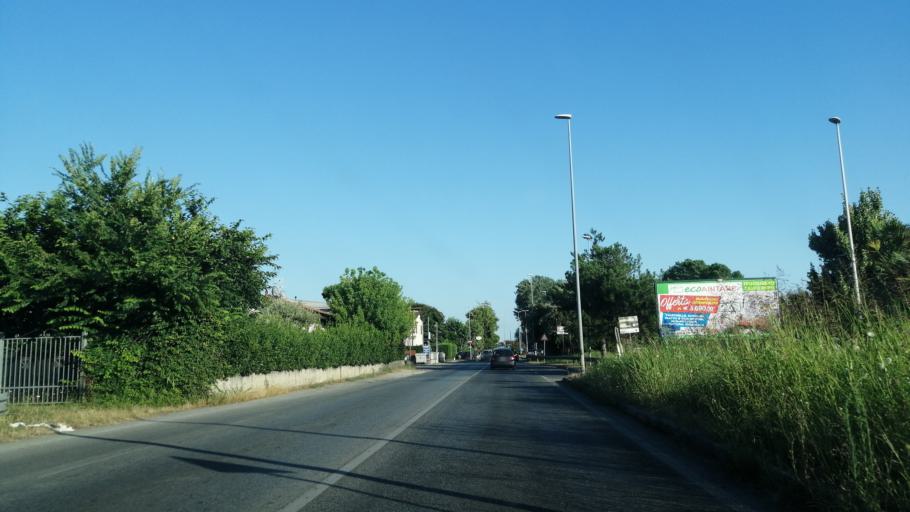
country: IT
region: Tuscany
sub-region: Provincia di Lucca
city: Camaiore
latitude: 43.9120
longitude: 10.2234
